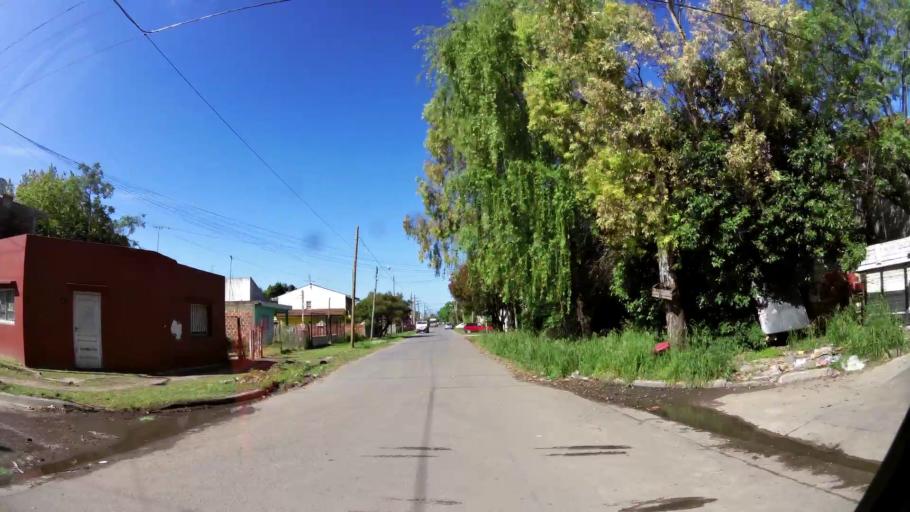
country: AR
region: Buenos Aires
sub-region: Partido de Quilmes
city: Quilmes
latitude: -34.8022
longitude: -58.2481
